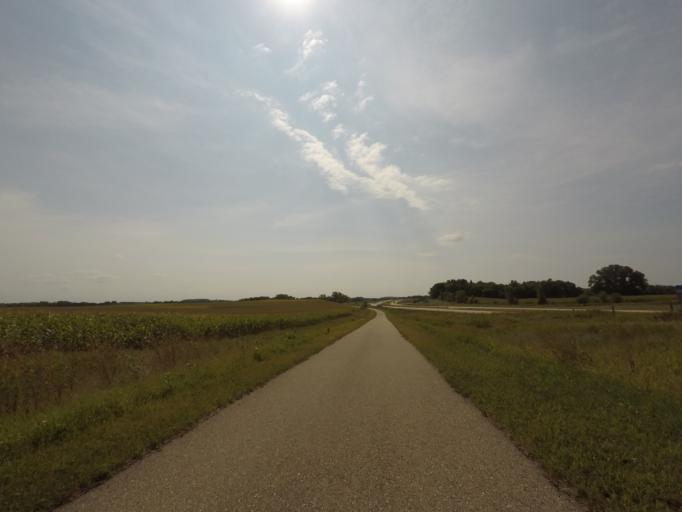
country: US
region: Wisconsin
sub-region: Jefferson County
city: Jefferson
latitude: 42.9840
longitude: -88.8281
